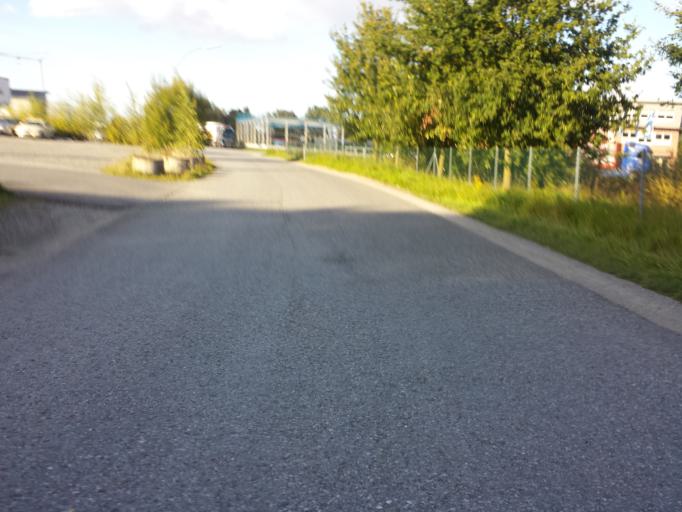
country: DE
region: North Rhine-Westphalia
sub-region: Regierungsbezirk Detmold
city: Langenberg
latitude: 51.7575
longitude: 8.3286
